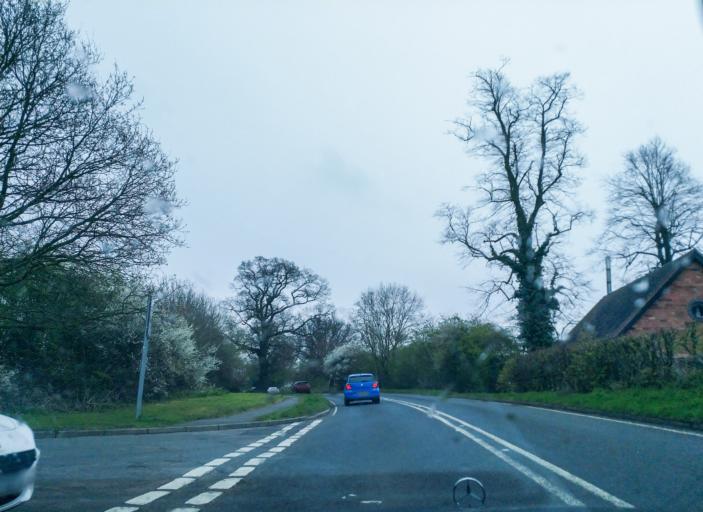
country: GB
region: England
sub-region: Warwickshire
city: Warwick
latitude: 52.2725
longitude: -1.6308
